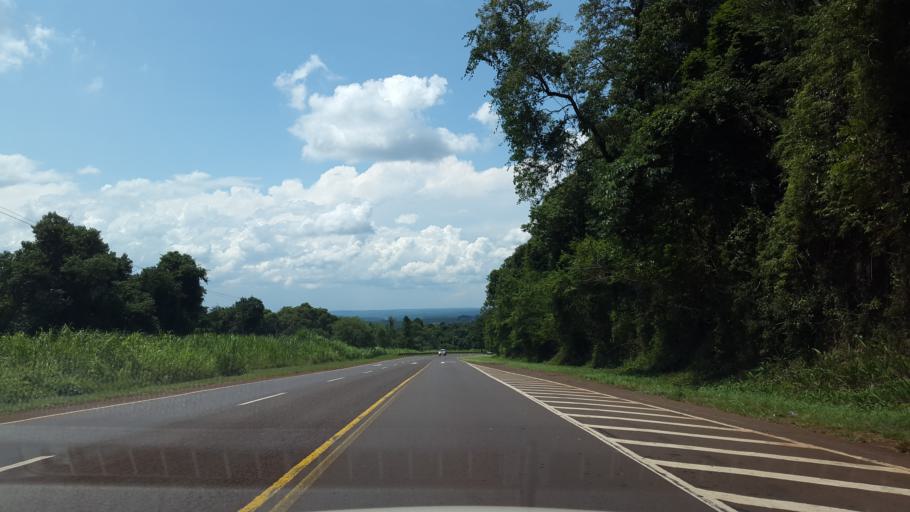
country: AR
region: Misiones
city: El Alcazar
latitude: -26.7246
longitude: -54.8658
